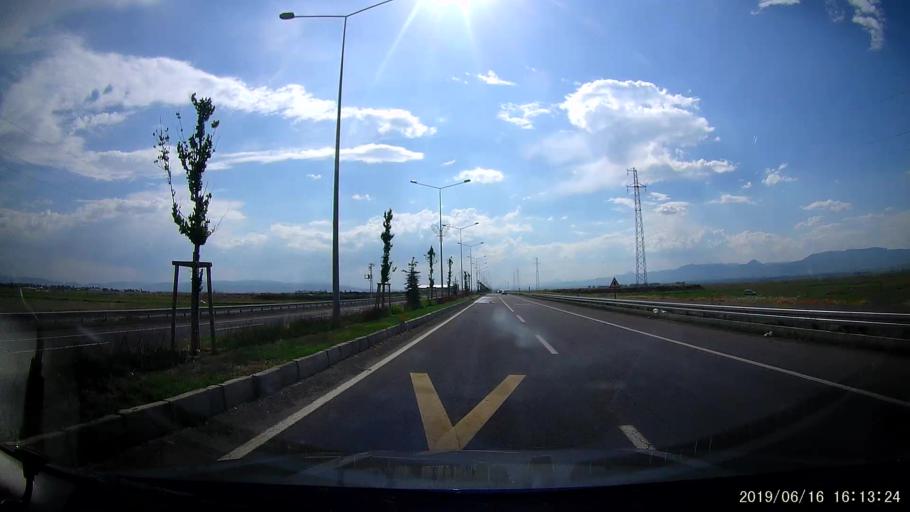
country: TR
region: Erzurum
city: Erzurum
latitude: 39.9595
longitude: 41.2729
